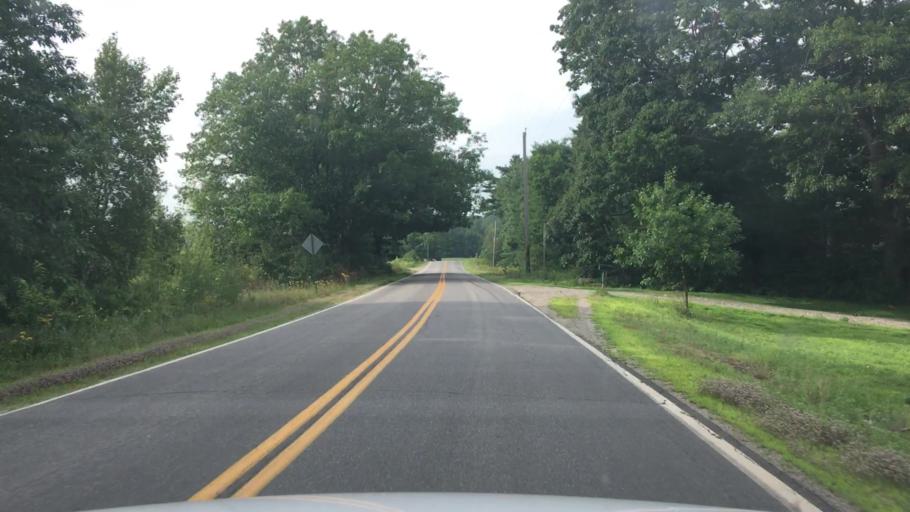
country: US
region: Maine
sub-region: Knox County
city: Washington
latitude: 44.2066
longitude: -69.3818
